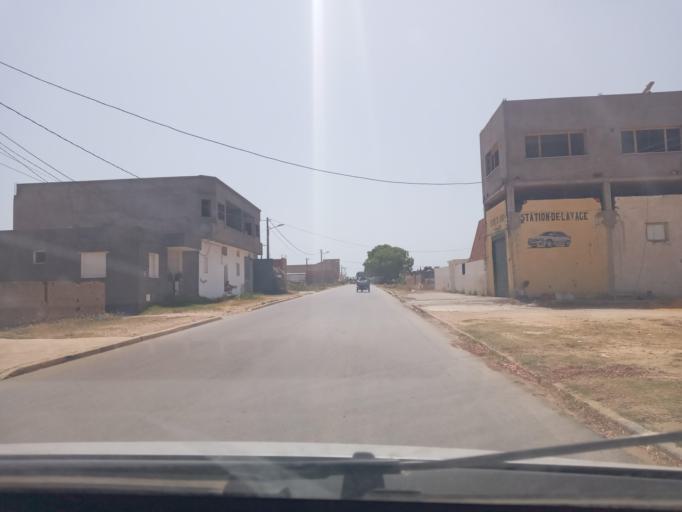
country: TN
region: Nabul
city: El Haouaria
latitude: 37.0438
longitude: 11.0251
